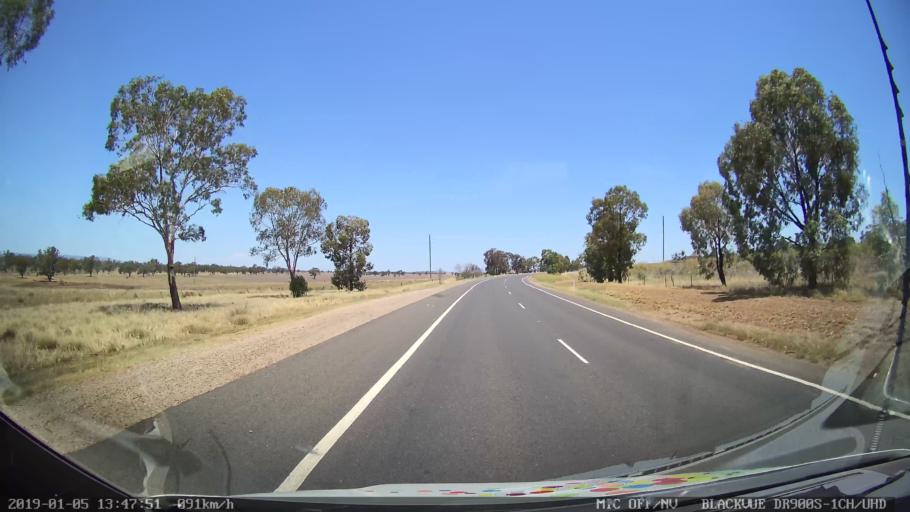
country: AU
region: New South Wales
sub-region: Gunnedah
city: Gunnedah
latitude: -30.9933
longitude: 150.2793
